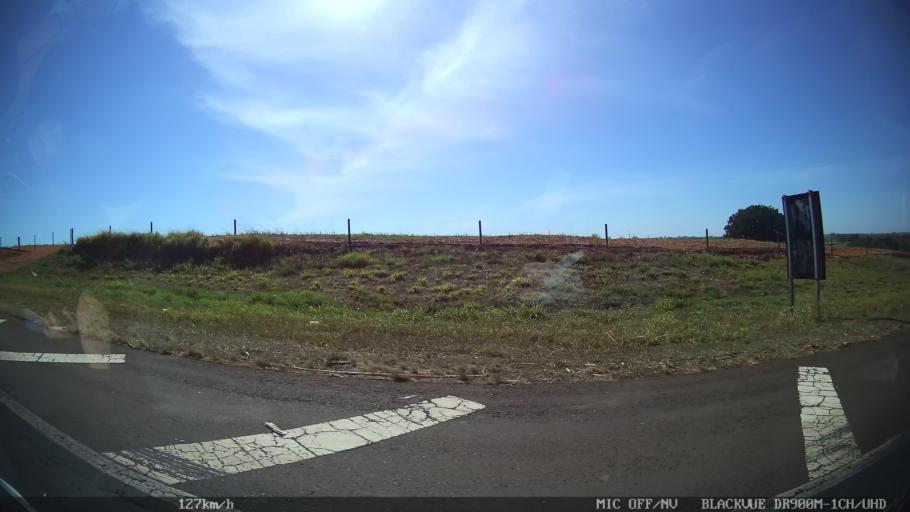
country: BR
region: Sao Paulo
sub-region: Olimpia
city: Olimpia
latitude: -20.6238
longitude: -48.7772
